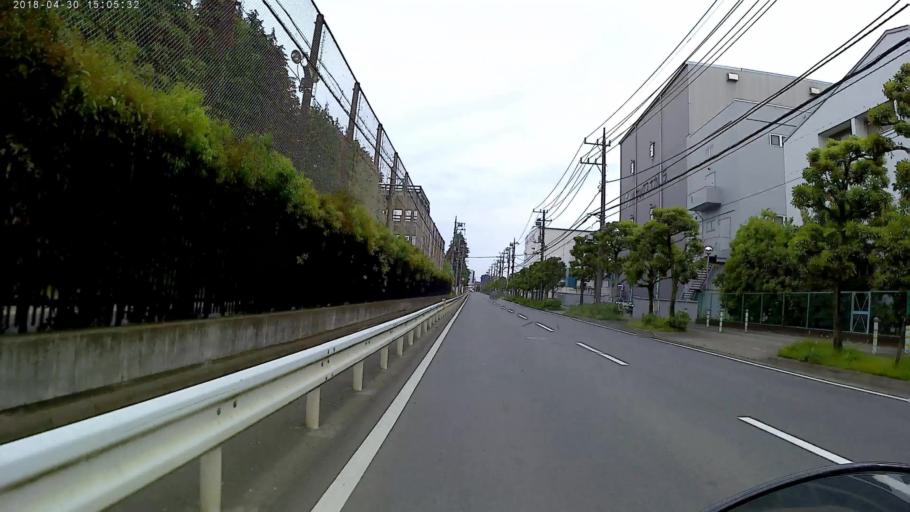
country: JP
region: Kanagawa
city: Zama
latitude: 35.5593
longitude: 139.3413
